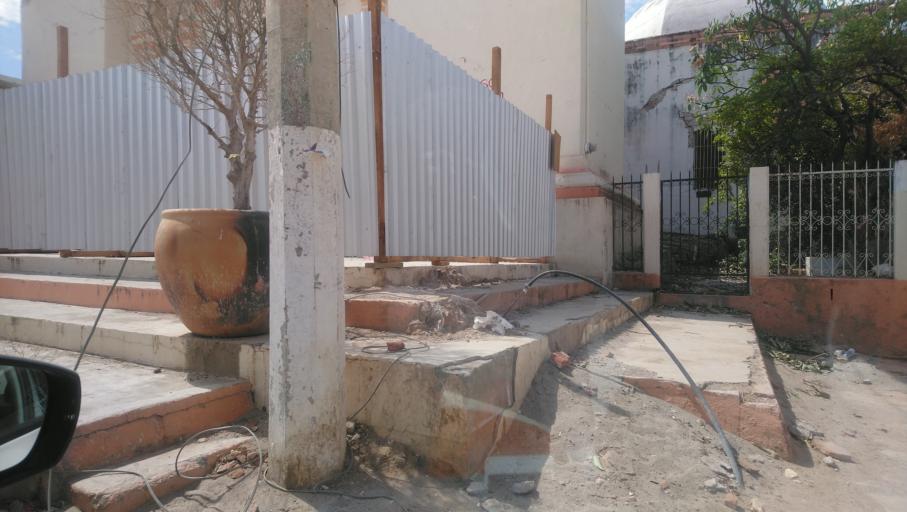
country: MX
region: Oaxaca
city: San Blas Atempa
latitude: 16.3356
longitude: -95.2315
